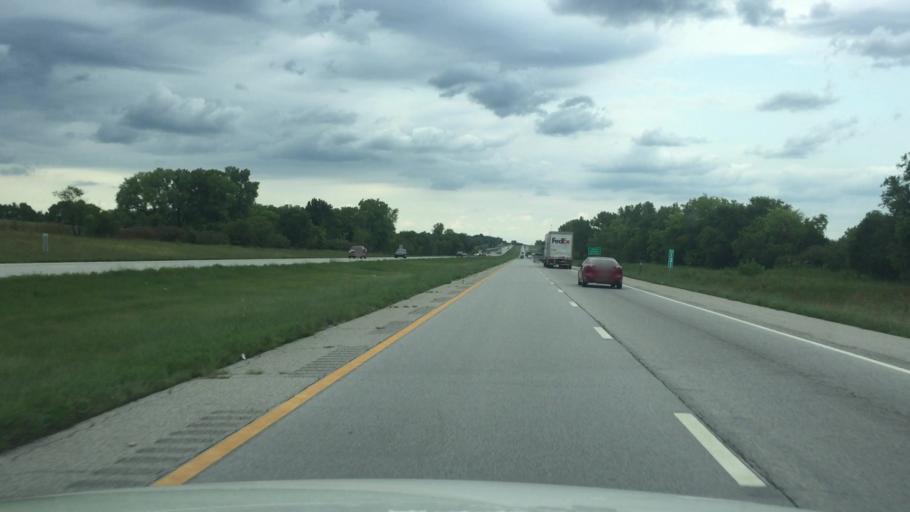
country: US
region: Kansas
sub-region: Miami County
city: Louisburg
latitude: 38.7563
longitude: -94.6775
